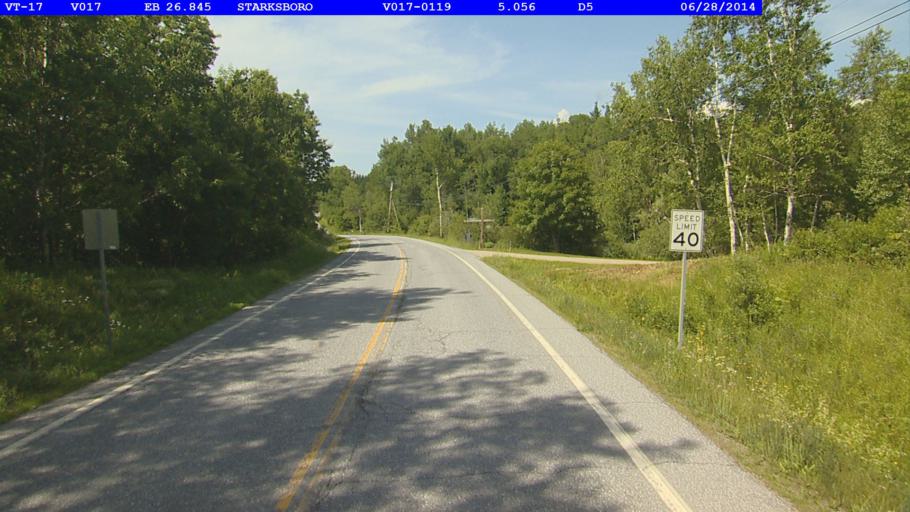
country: US
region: Vermont
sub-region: Addison County
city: Bristol
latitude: 44.2119
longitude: -72.9649
